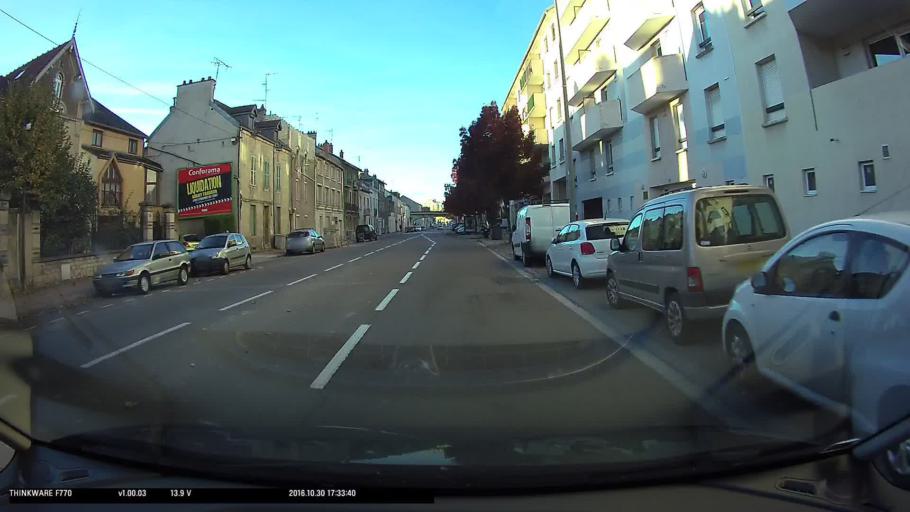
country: FR
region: Bourgogne
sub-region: Departement de la Cote-d'Or
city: Longvic
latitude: 47.3100
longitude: 5.0543
